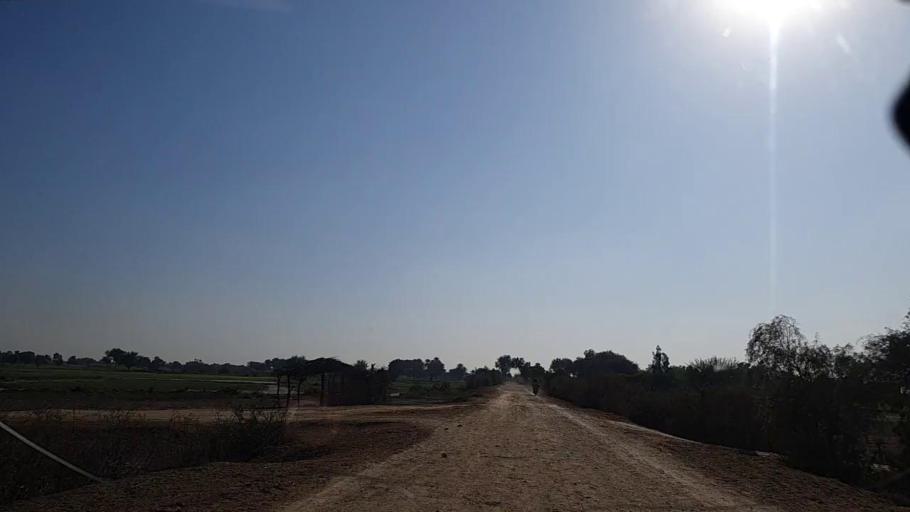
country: PK
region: Sindh
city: Khanpur
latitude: 27.7897
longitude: 69.3700
